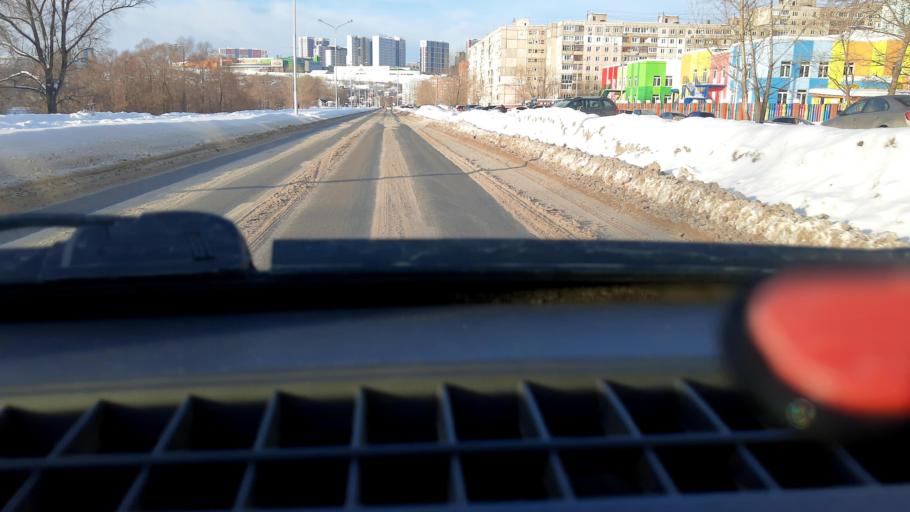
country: RU
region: Bashkortostan
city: Ufa
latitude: 54.7596
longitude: 56.0638
